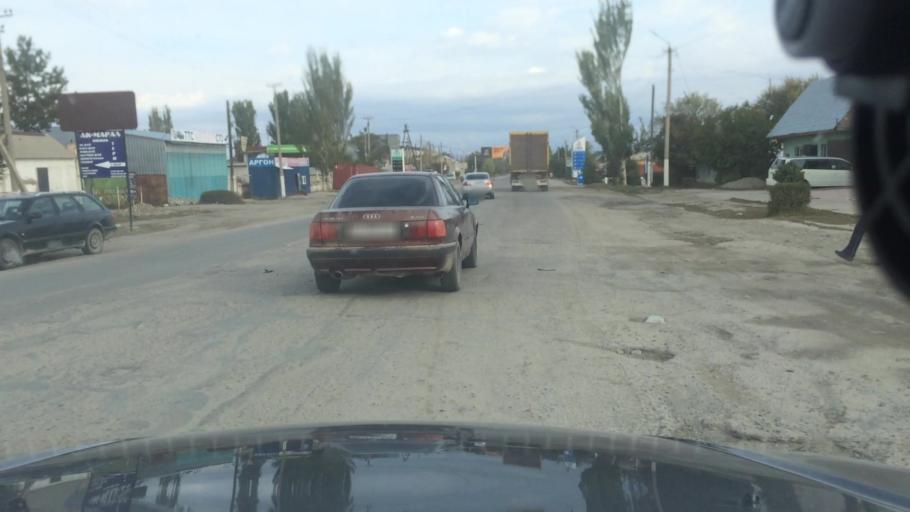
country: KG
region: Ysyk-Koel
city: Karakol
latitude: 42.5117
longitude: 78.3857
